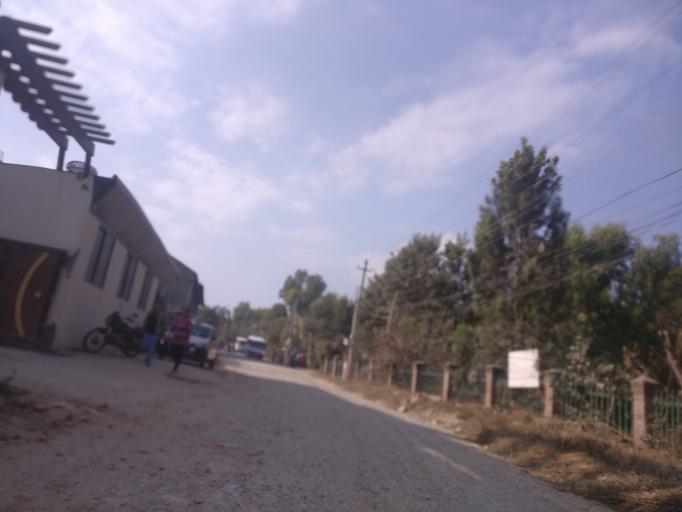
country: NP
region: Central Region
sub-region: Bagmati Zone
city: Patan
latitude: 27.6842
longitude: 85.3274
